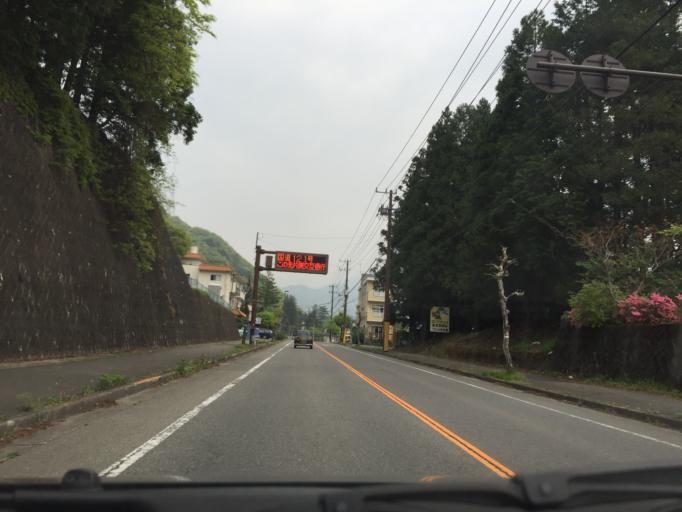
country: JP
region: Tochigi
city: Imaichi
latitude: 36.8332
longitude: 139.7169
